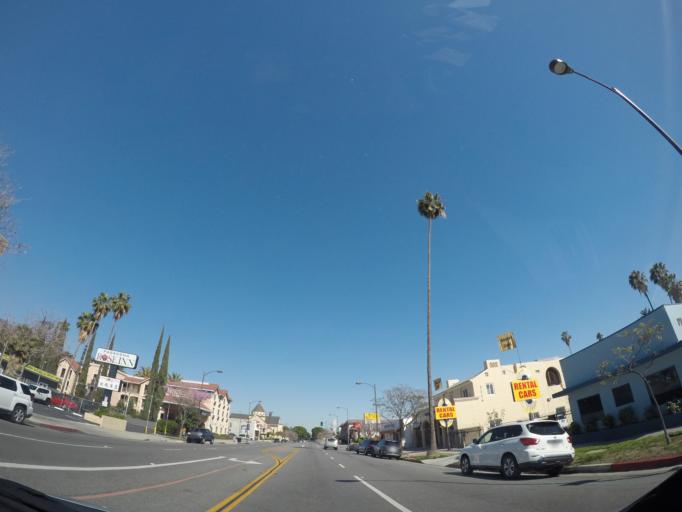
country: US
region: California
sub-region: Los Angeles County
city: East Pasadena
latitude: 34.1461
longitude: -118.1071
